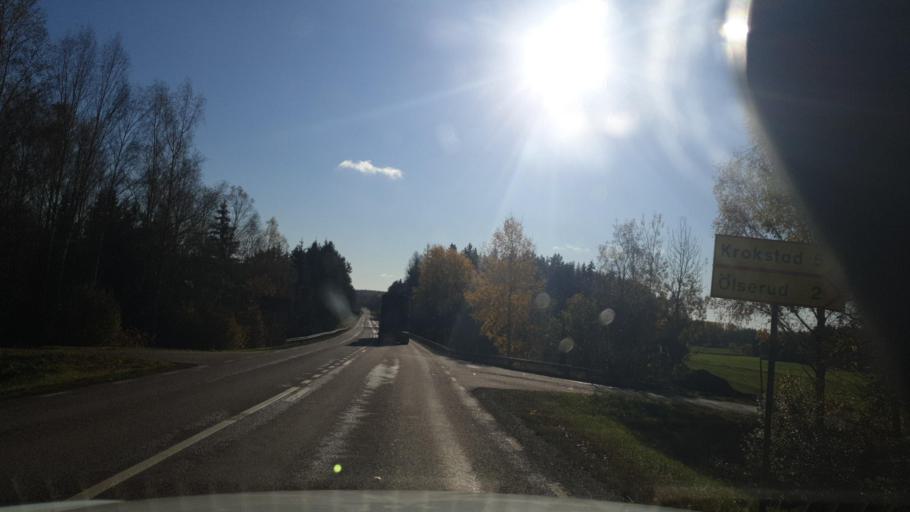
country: SE
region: Vaermland
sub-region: Karlstads Kommun
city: Edsvalla
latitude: 59.5647
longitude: 13.0264
